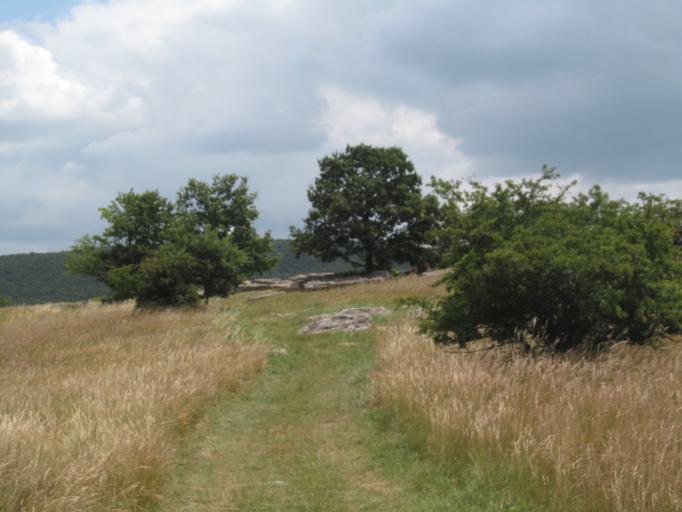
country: HU
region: Veszprem
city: Revfueloep
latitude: 46.8529
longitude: 17.6076
